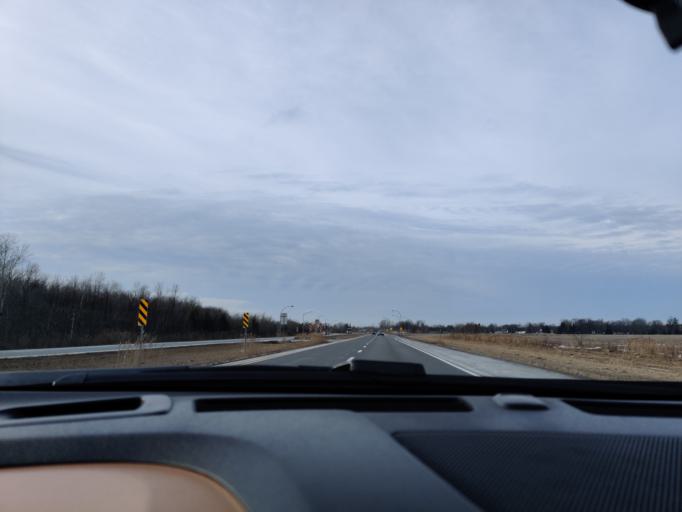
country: CA
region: Quebec
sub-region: Monteregie
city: Les Coteaux
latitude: 45.2243
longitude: -74.3143
